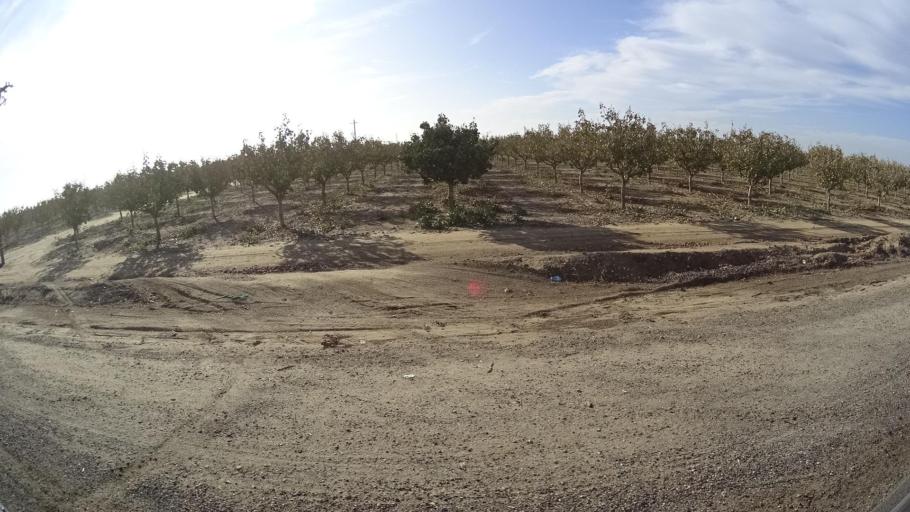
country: US
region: California
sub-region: Kern County
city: McFarland
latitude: 35.6020
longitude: -119.1782
